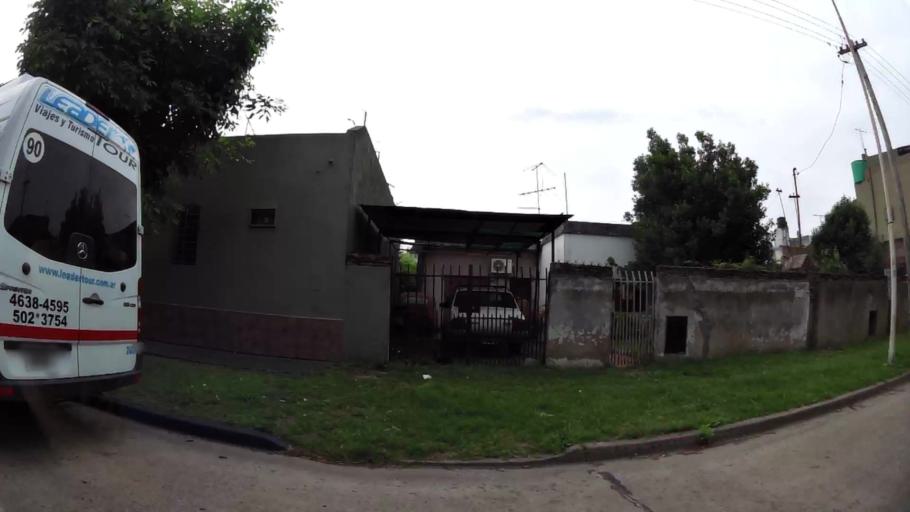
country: AR
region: Buenos Aires
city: San Justo
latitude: -34.6925
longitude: -58.5185
